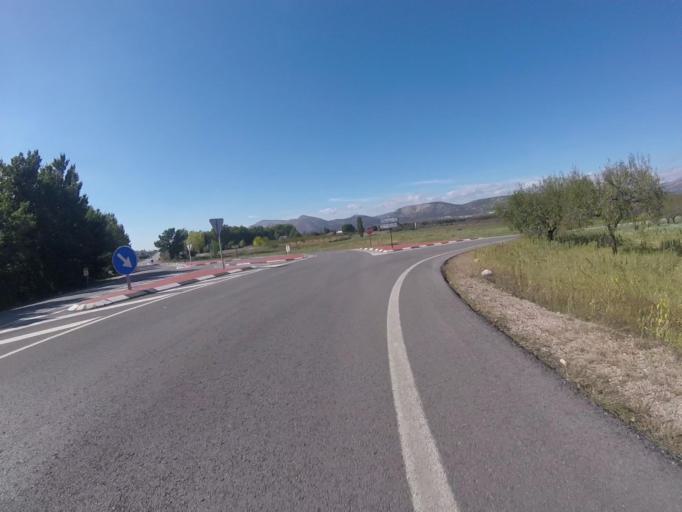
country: ES
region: Valencia
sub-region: Provincia de Castello
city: Albocasser
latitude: 40.3462
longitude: -0.0036
